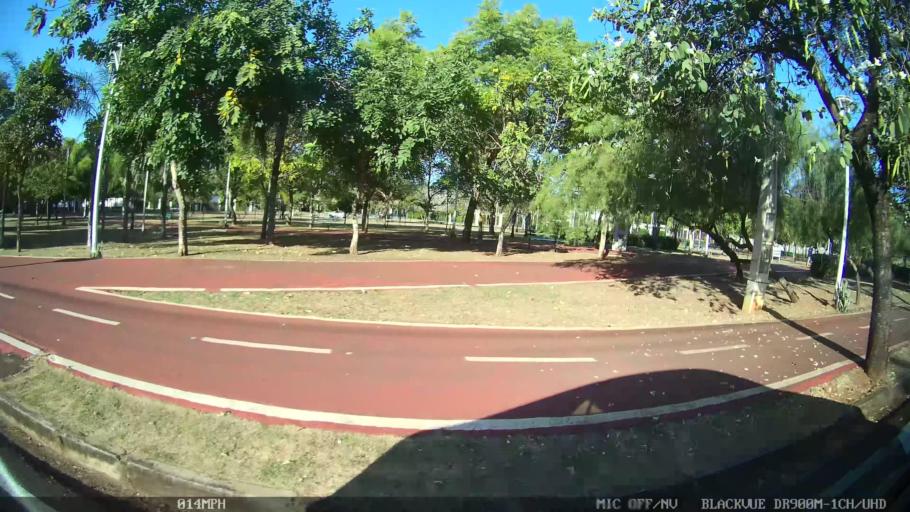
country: BR
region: Sao Paulo
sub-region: Sao Jose Do Rio Preto
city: Sao Jose do Rio Preto
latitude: -20.8494
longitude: -49.4131
